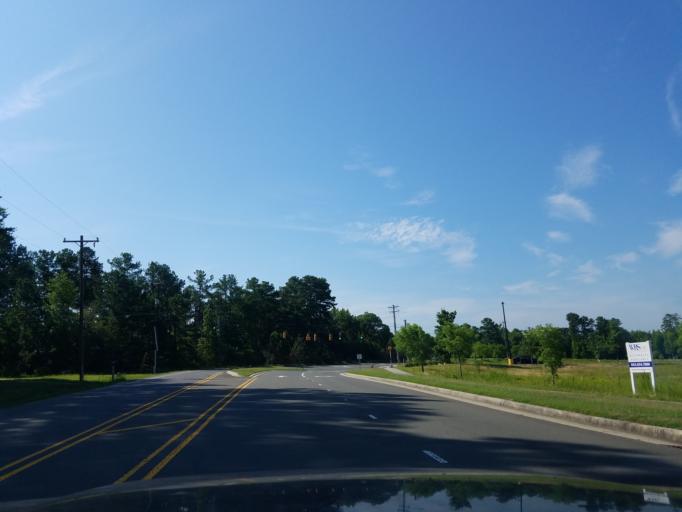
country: US
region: North Carolina
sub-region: Durham County
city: Gorman
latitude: 36.0299
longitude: -78.8401
